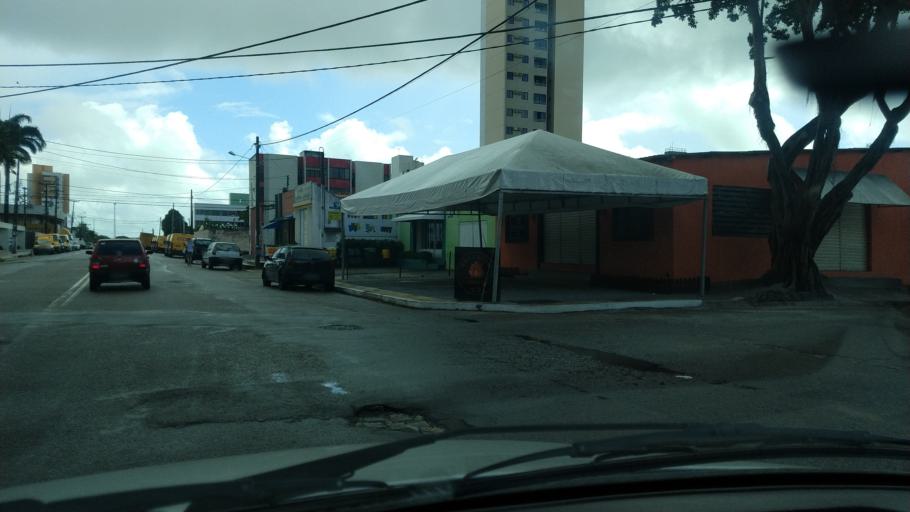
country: BR
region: Rio Grande do Norte
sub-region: Natal
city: Natal
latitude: -5.8129
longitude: -35.2193
